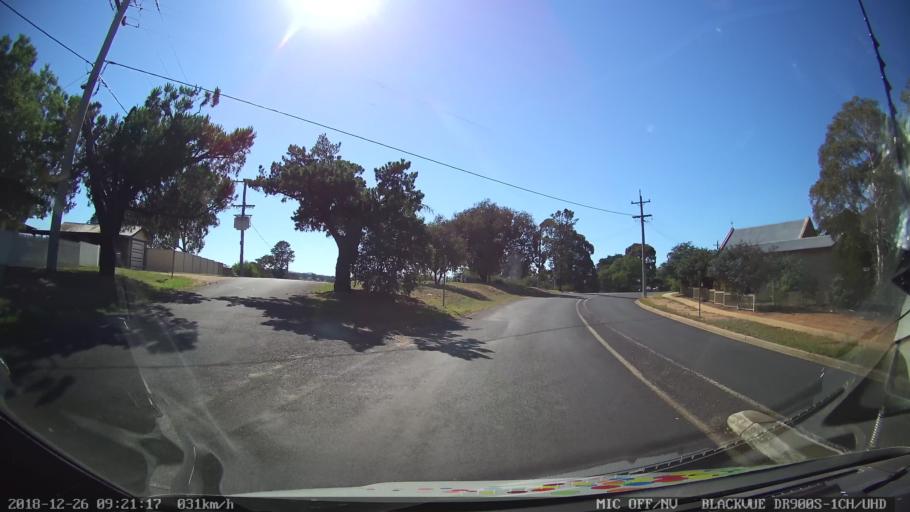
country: AU
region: New South Wales
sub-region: Mid-Western Regional
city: Kandos
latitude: -32.7995
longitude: 149.9726
